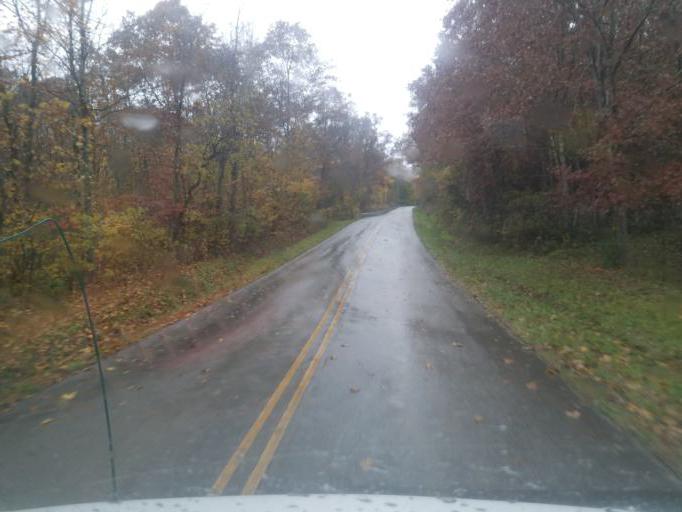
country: US
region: Ohio
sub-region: Washington County
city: Beverly
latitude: 39.4323
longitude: -81.6190
